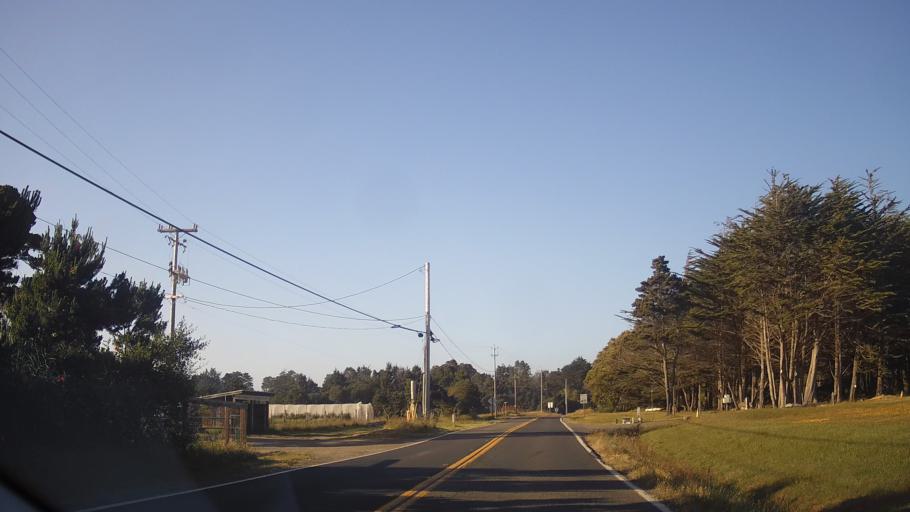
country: US
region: California
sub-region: Mendocino County
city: Fort Bragg
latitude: 39.4777
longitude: -123.7977
